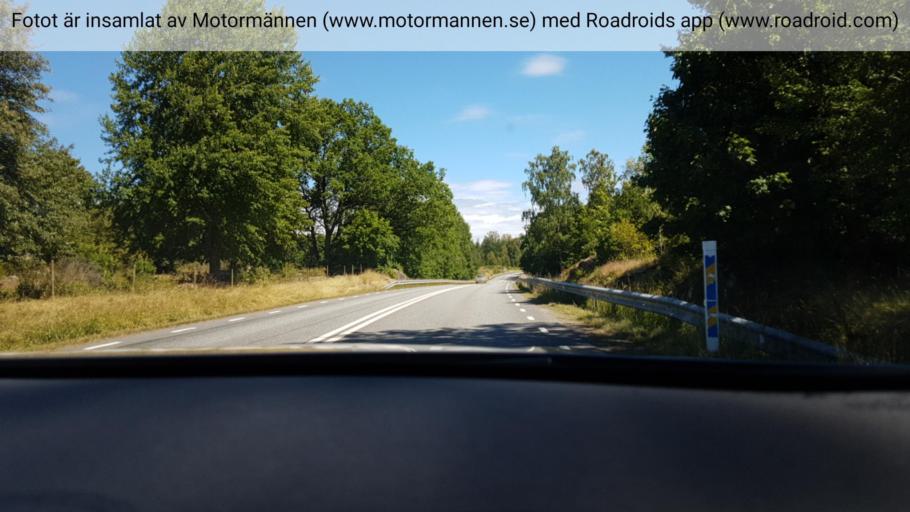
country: SE
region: Joenkoeping
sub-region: Jonkopings Kommun
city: Asa
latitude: 58.0070
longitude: 14.6265
